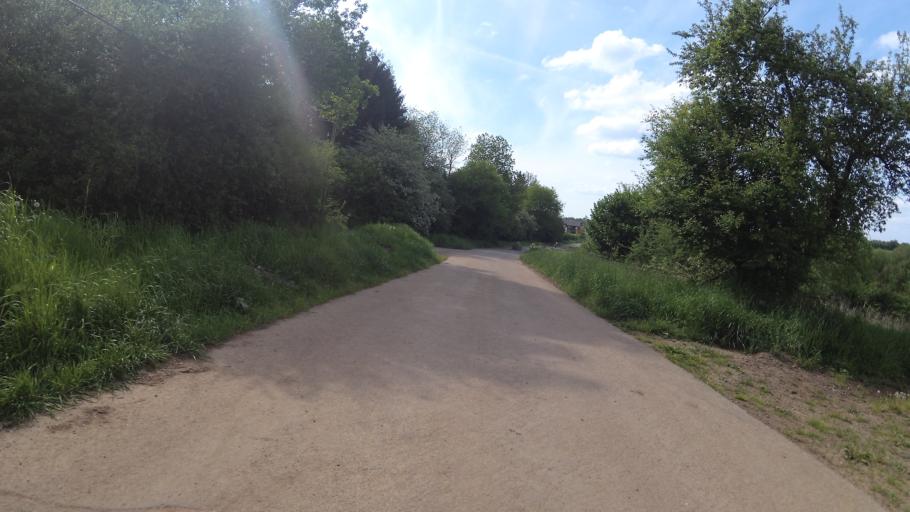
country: DE
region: Saarland
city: Sankt Wendel
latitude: 49.4477
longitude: 7.1592
